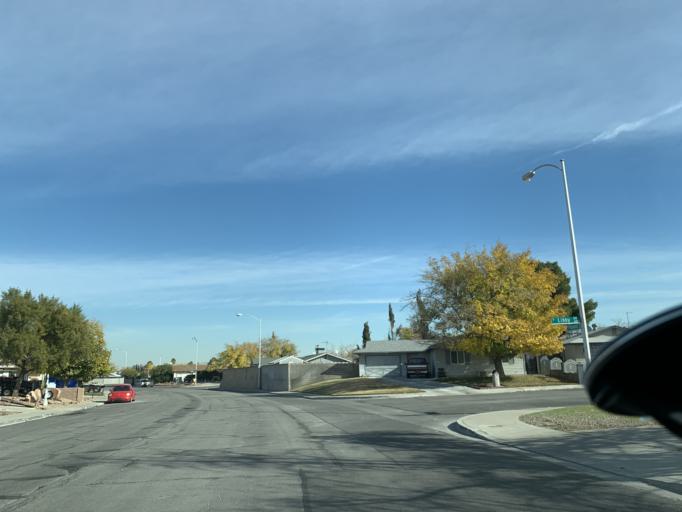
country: US
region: Nevada
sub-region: Clark County
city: Spring Valley
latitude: 36.1084
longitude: -115.2316
